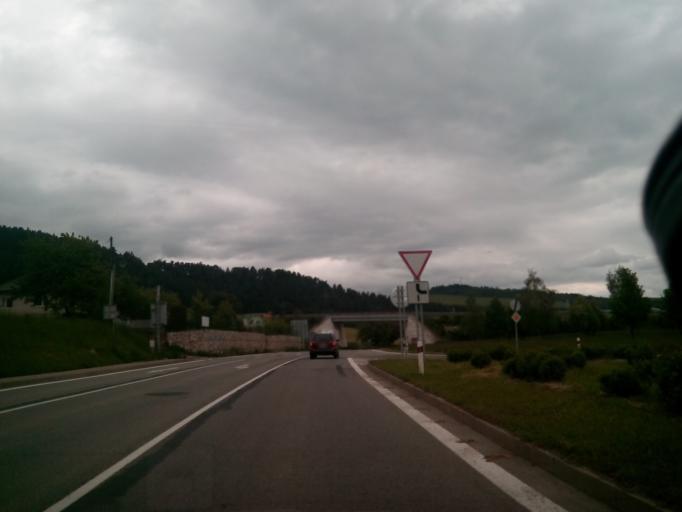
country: SK
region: Kosicky
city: Krompachy
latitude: 49.0084
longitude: 20.9421
